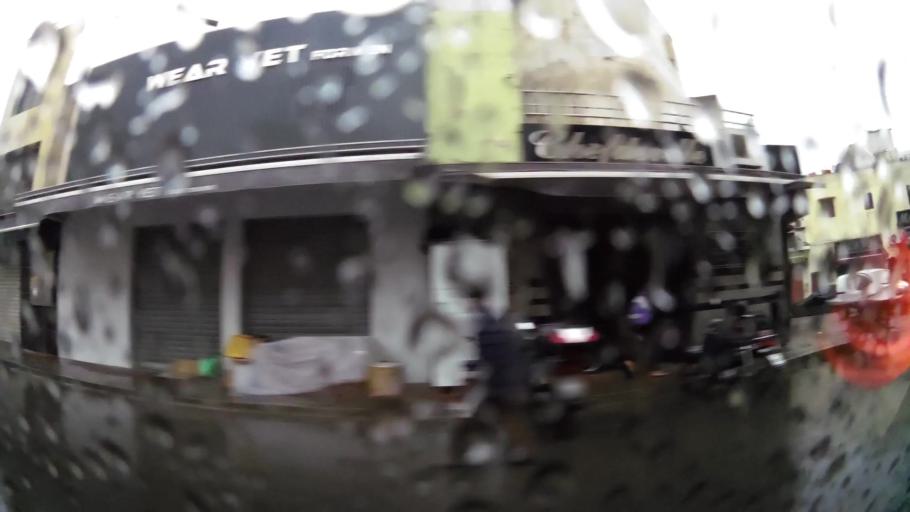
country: MA
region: Grand Casablanca
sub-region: Casablanca
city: Casablanca
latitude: 33.5652
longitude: -7.6023
